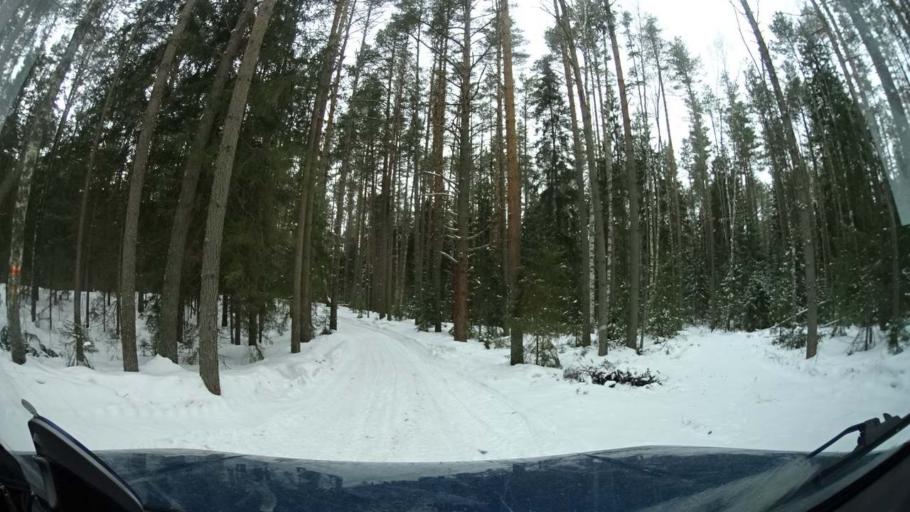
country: RU
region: Tverskaya
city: Radchenko
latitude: 56.6924
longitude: 36.4312
